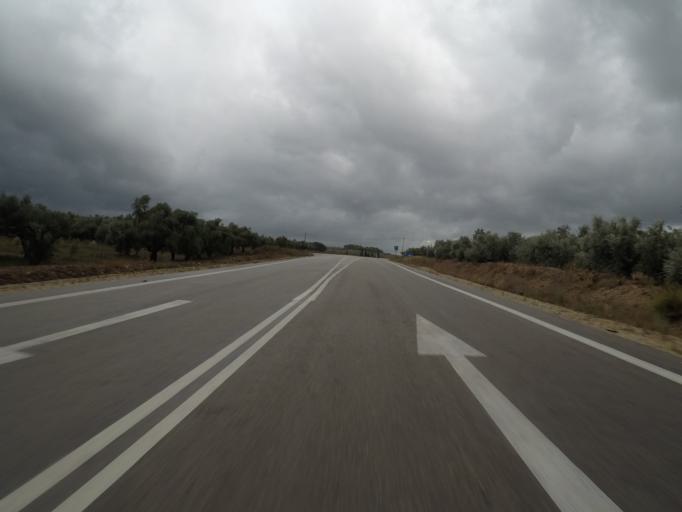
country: GR
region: Peloponnese
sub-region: Nomos Messinias
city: Gargalianoi
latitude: 37.0119
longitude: 21.6539
